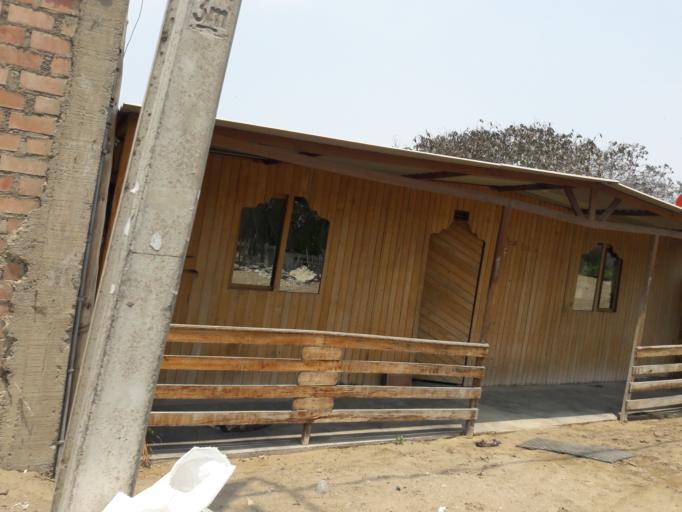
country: PE
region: Lima
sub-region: Lima
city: Santa Rosa
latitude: -11.7720
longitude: -77.1629
